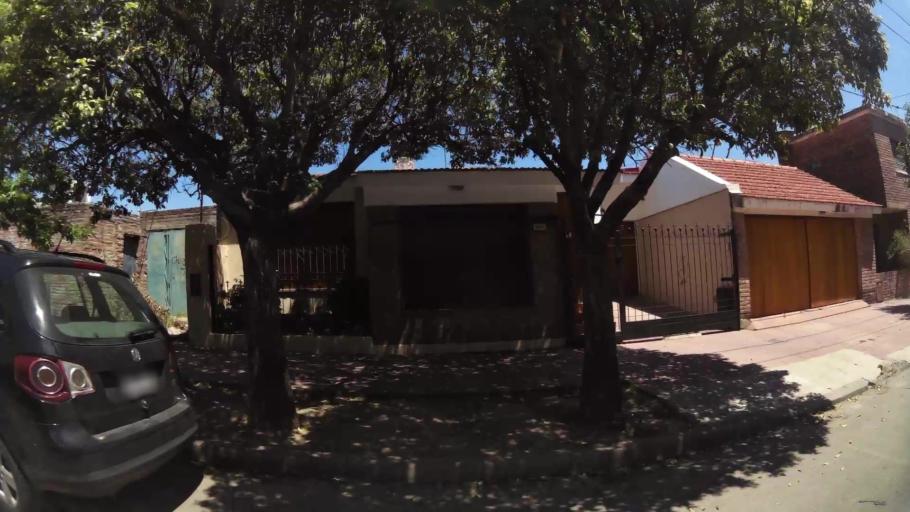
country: AR
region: Cordoba
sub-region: Departamento de Capital
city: Cordoba
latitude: -31.4121
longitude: -64.2172
